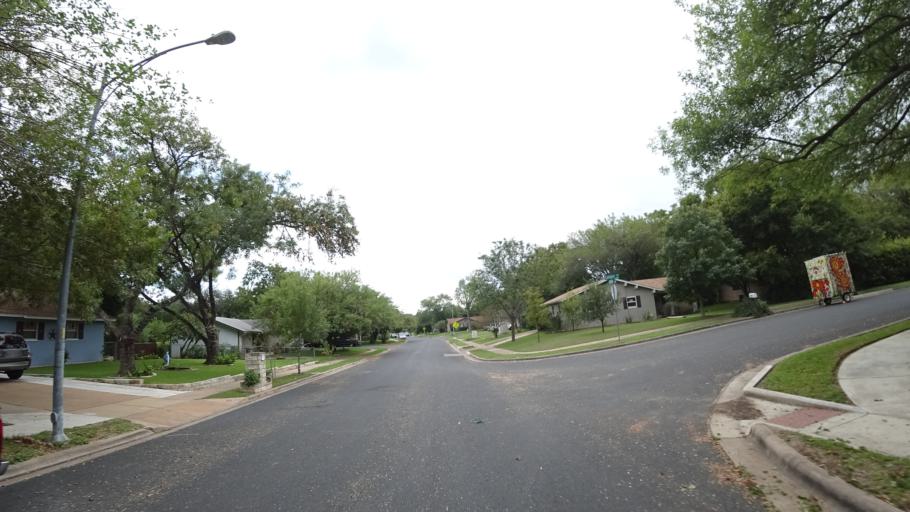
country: US
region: Texas
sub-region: Travis County
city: Rollingwood
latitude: 30.2163
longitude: -97.7801
